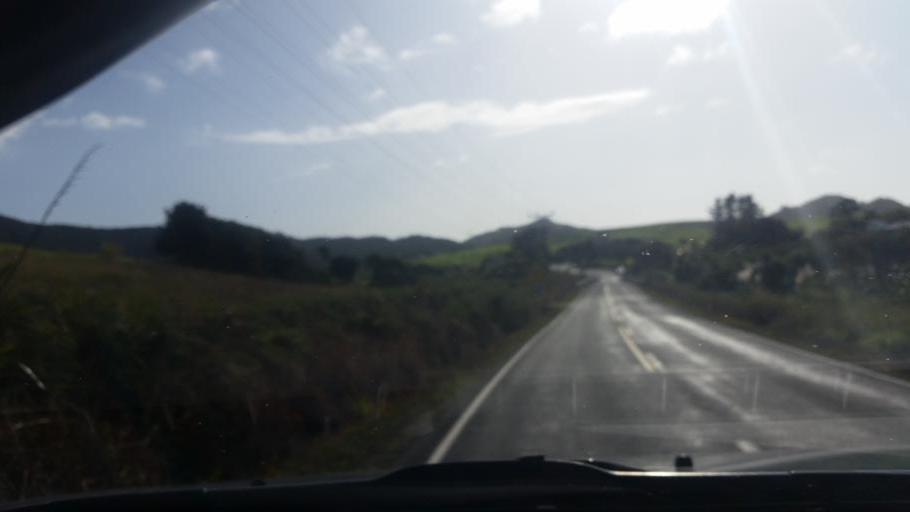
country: NZ
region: Auckland
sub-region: Auckland
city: Wellsford
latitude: -36.0846
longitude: 174.5701
